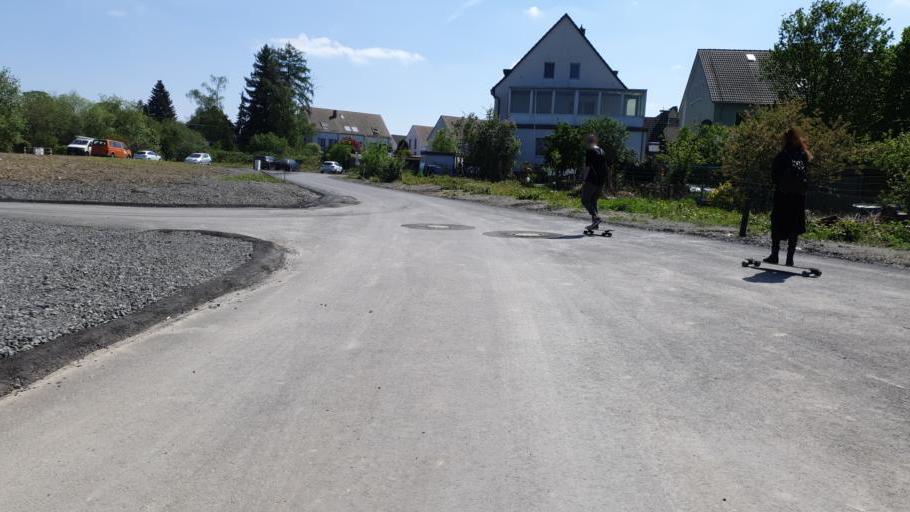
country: DE
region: North Rhine-Westphalia
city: Opladen
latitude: 51.0432
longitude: 7.0466
